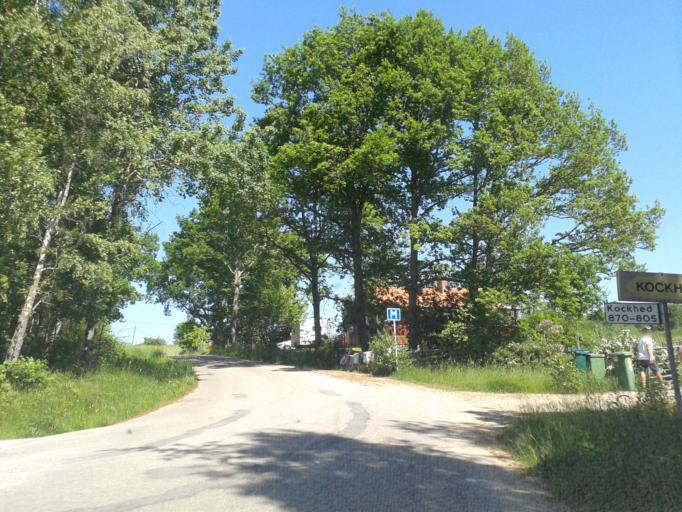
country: SE
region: Vaestra Goetaland
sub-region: Orust
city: Henan
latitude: 58.2681
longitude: 11.7577
